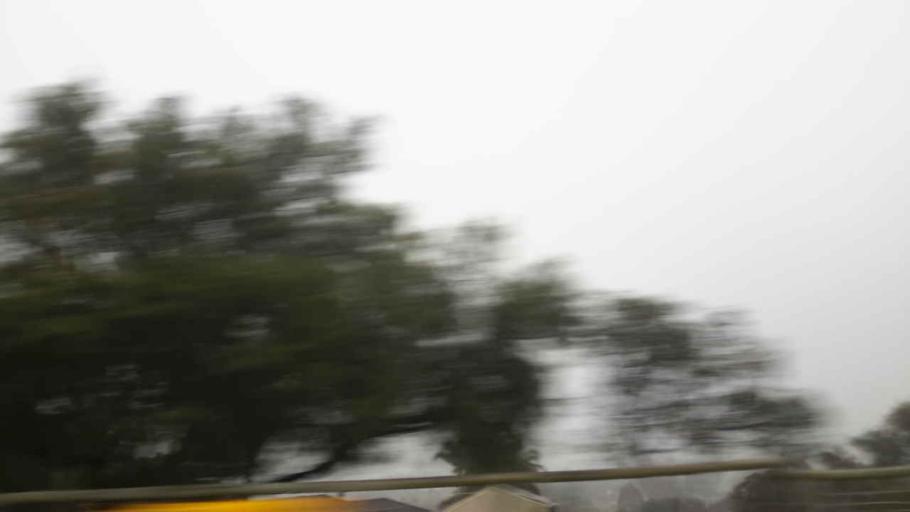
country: AU
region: New South Wales
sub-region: Wollondilly
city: Douglas Park
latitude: -34.1507
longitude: 150.7224
